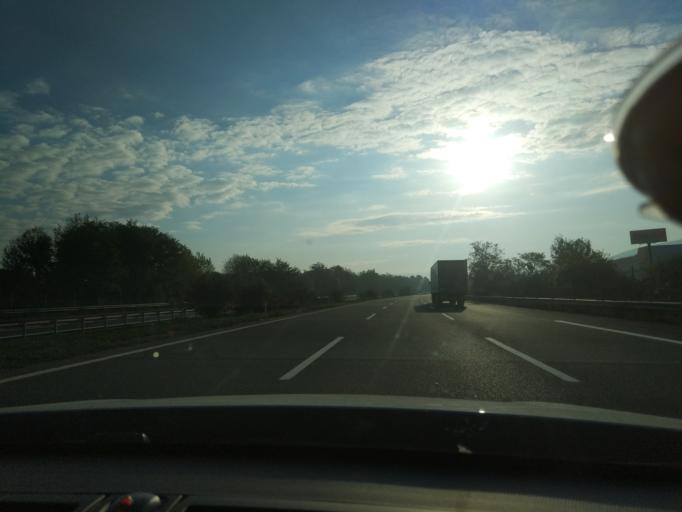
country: TR
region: Duzce
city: Duzce
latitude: 40.8038
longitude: 31.1697
